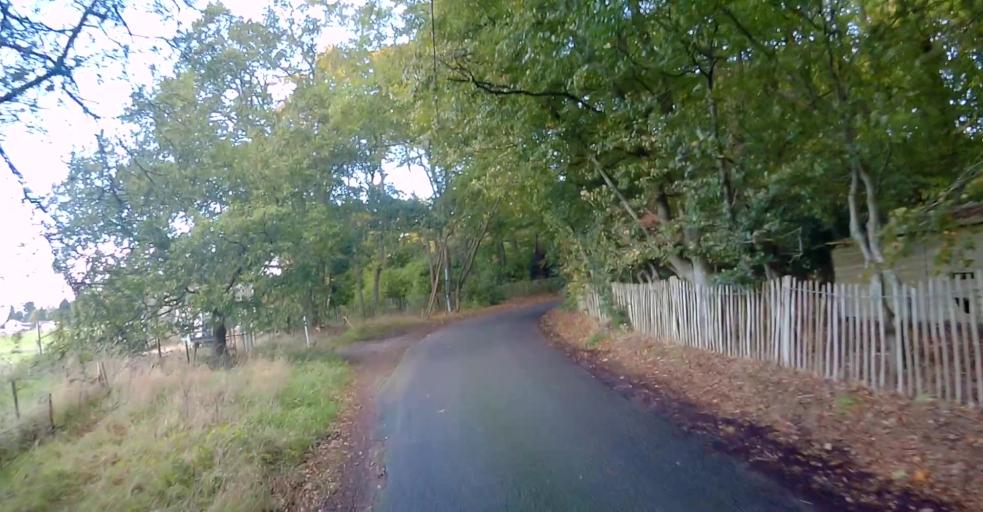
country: GB
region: England
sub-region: Surrey
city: Elstead
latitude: 51.1908
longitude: -0.7382
